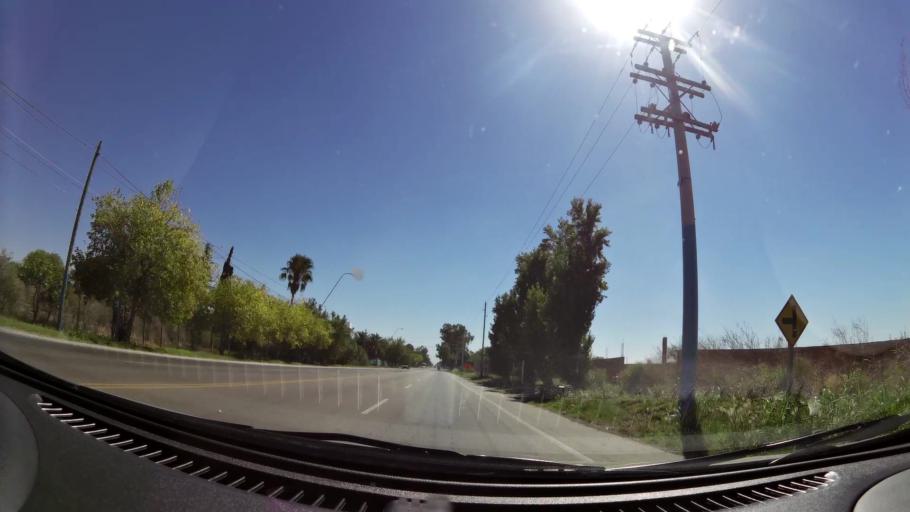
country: AR
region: San Juan
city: Villa Aberastain
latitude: -31.6196
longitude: -68.5499
